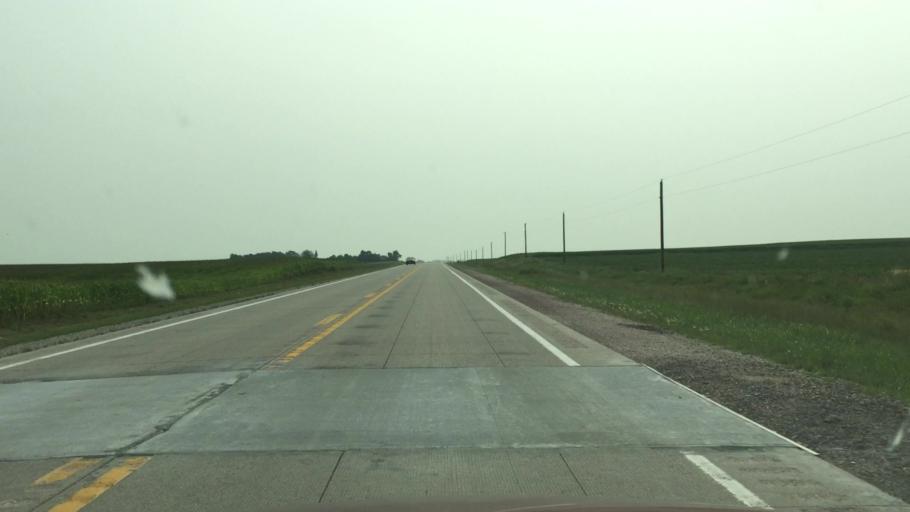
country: US
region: Iowa
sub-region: Osceola County
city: Sibley
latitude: 43.4328
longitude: -95.6362
